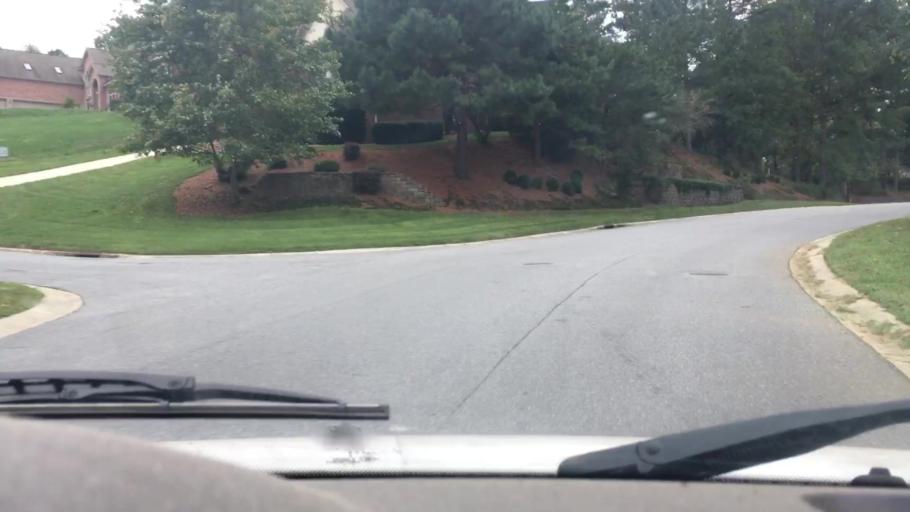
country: US
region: North Carolina
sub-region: Lincoln County
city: Denver
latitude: 35.4816
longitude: -81.0278
